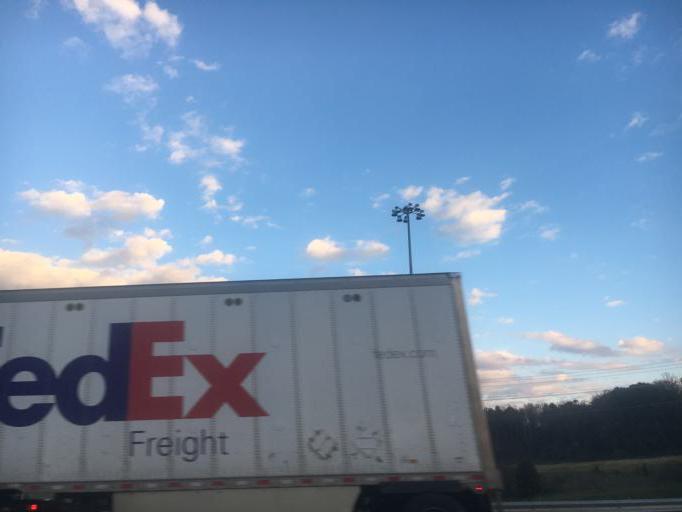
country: US
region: Tennessee
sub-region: Washington County
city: Gray
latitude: 36.4065
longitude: -82.4772
